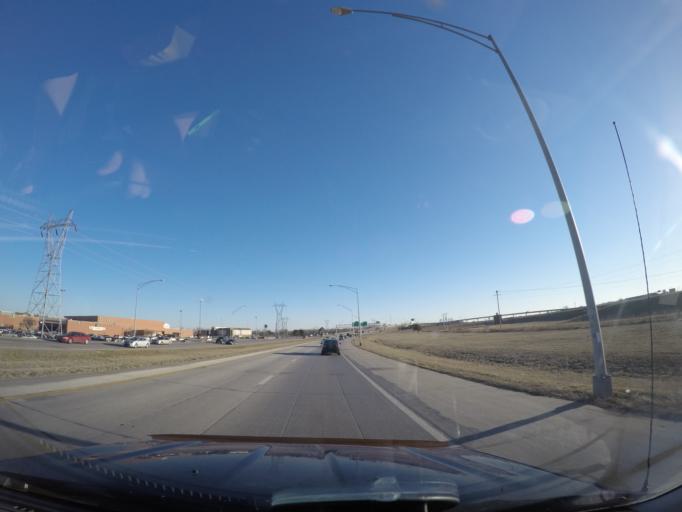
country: US
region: Kansas
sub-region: Sedgwick County
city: Wichita
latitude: 37.6777
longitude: -97.4029
